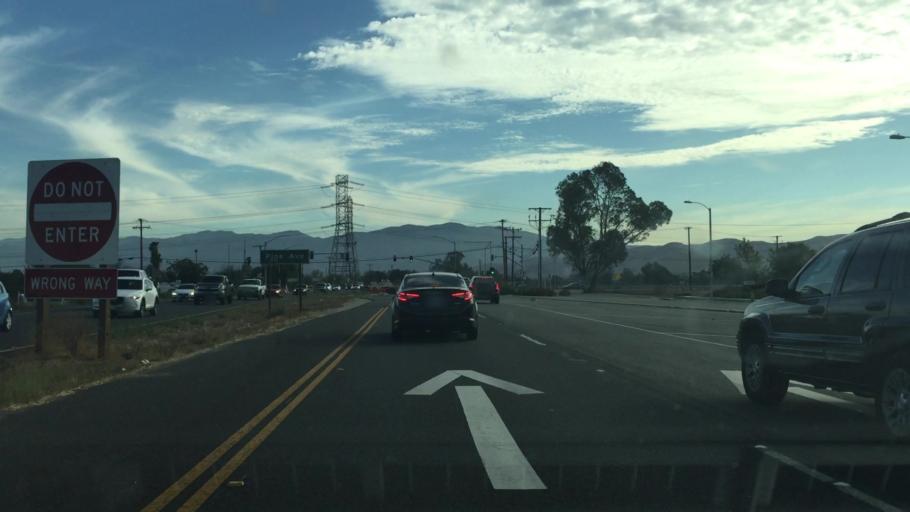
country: US
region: California
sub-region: San Bernardino County
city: Los Serranos
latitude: 33.9549
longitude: -117.6505
